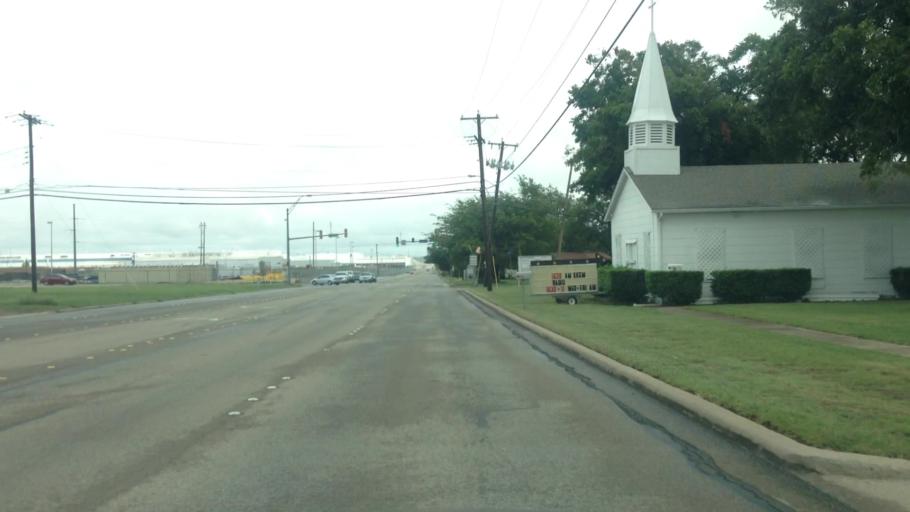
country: US
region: Texas
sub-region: Tarrant County
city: White Settlement
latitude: 32.7655
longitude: -97.4617
